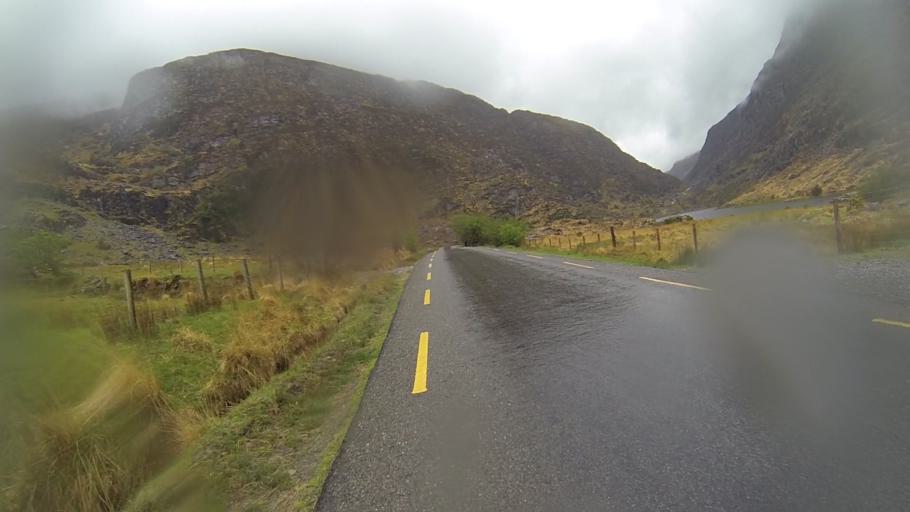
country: IE
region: Munster
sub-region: Ciarrai
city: Cill Airne
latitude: 52.0162
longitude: -9.6360
